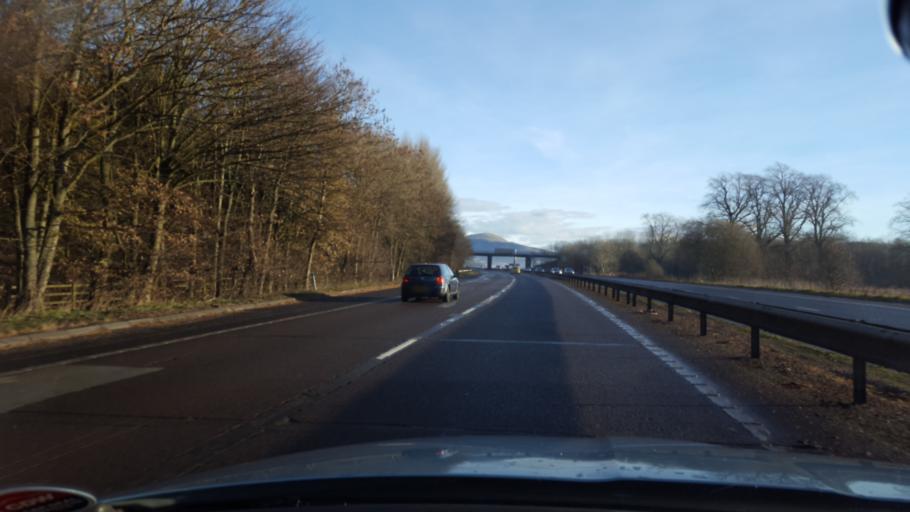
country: GB
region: Scotland
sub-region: Perth and Kinross
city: Milnathort
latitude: 56.2320
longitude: -3.4109
